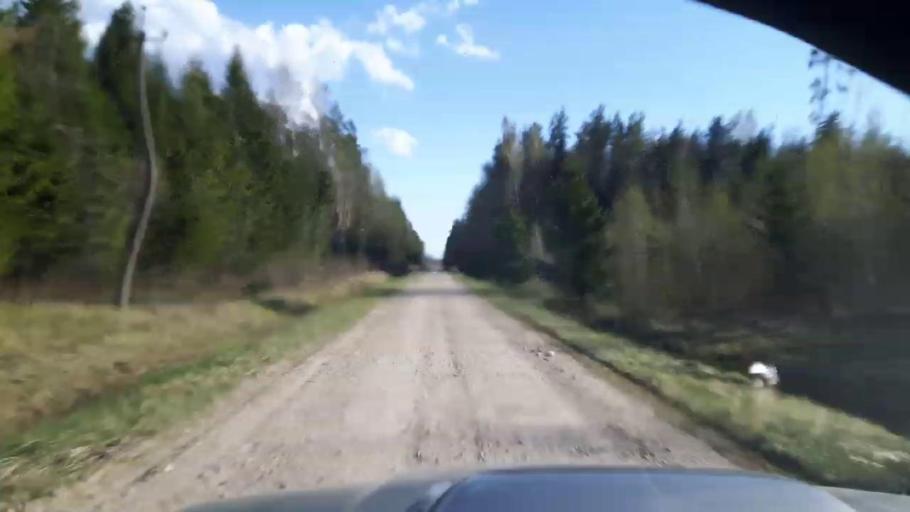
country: EE
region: Paernumaa
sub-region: Tootsi vald
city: Tootsi
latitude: 58.4254
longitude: 24.8515
